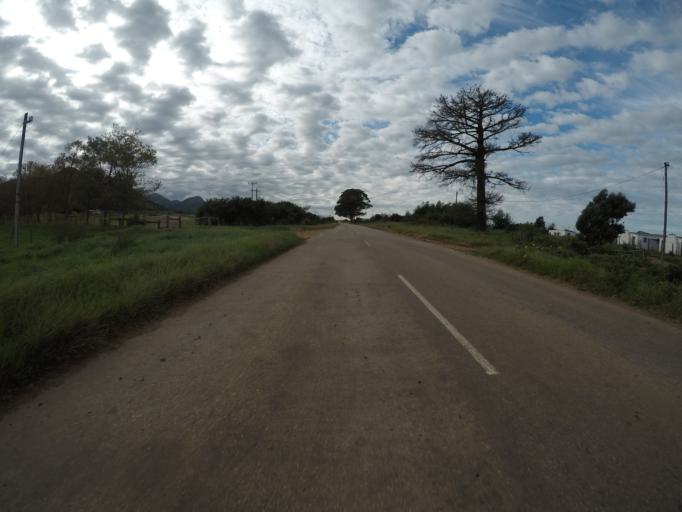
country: ZA
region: Eastern Cape
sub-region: Cacadu District Municipality
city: Kareedouw
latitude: -34.0098
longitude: 24.2743
